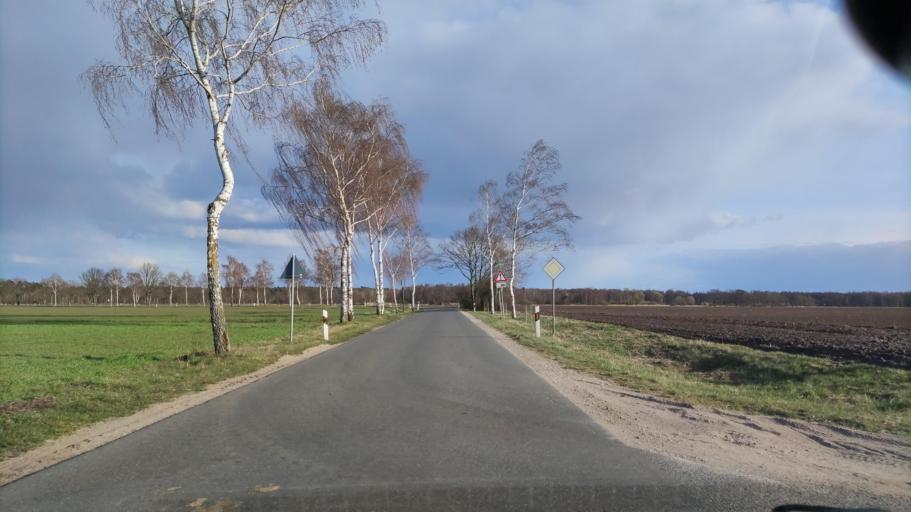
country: DE
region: Lower Saxony
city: Klein Gusborn
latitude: 53.0522
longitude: 11.2270
